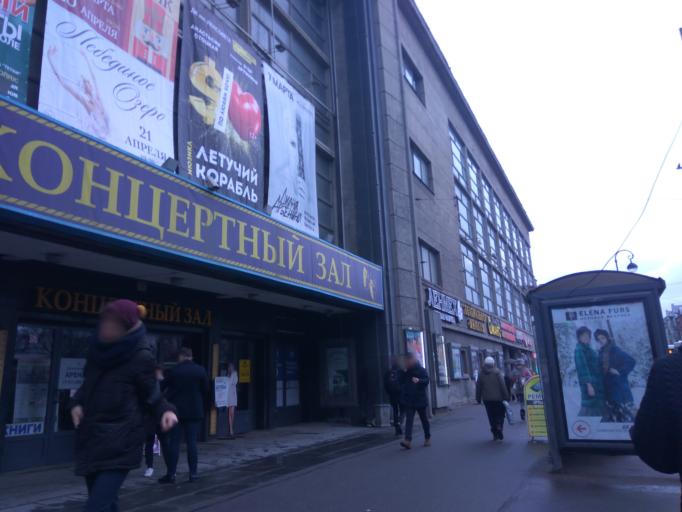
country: RU
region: St.-Petersburg
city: Petrogradka
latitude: 59.9670
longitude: 30.3103
